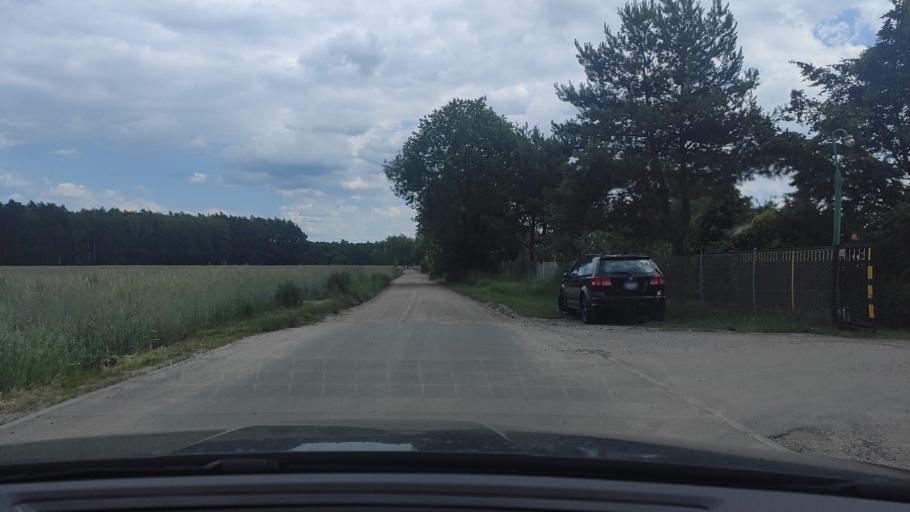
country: PL
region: Greater Poland Voivodeship
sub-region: Powiat poznanski
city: Pobiedziska
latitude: 52.4949
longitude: 17.1891
